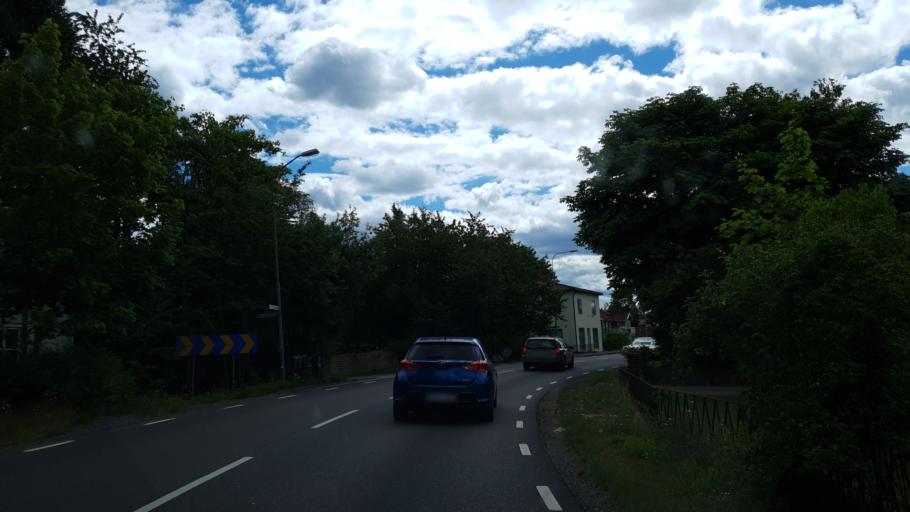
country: SE
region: Kalmar
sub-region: Emmaboda Kommun
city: Emmaboda
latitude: 56.9178
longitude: 15.5719
